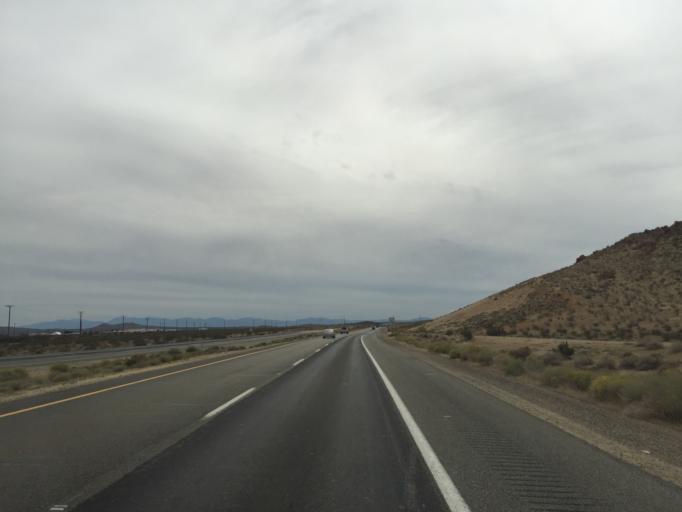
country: US
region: California
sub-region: Kern County
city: Mojave
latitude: 35.0051
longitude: -118.1604
